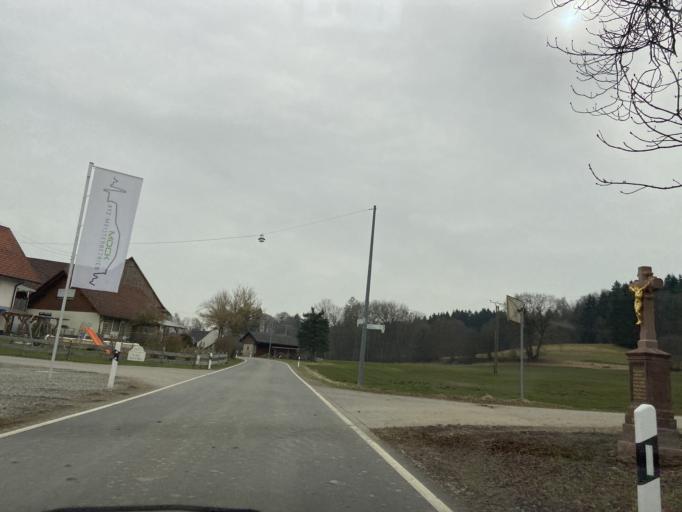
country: DE
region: Baden-Wuerttemberg
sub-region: Tuebingen Region
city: Illmensee
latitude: 47.8913
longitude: 9.3751
